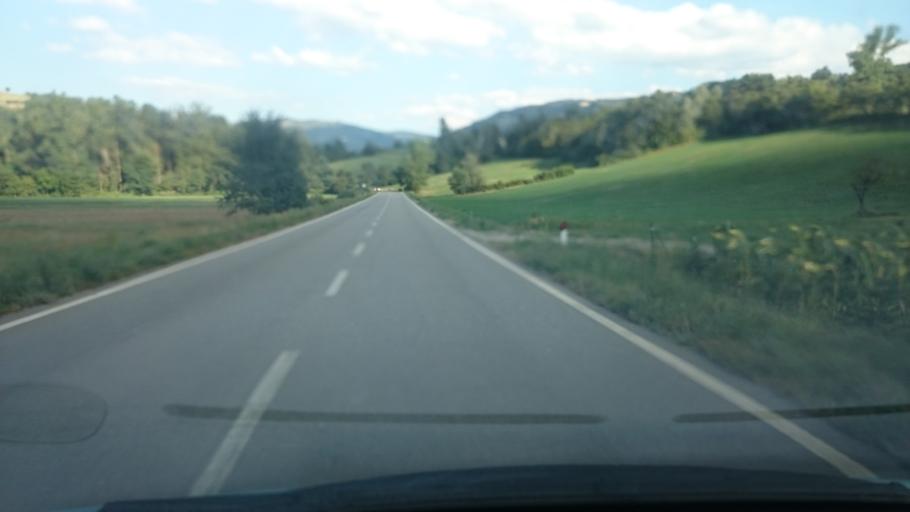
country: IT
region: Emilia-Romagna
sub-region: Provincia di Reggio Emilia
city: Toano
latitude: 44.4178
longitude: 10.5716
